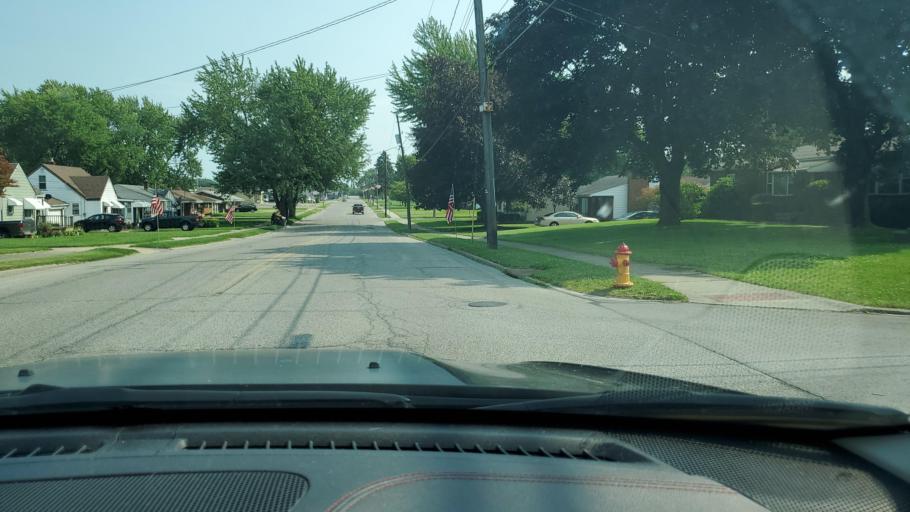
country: US
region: Ohio
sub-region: Mahoning County
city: Struthers
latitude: 41.0473
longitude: -80.6035
